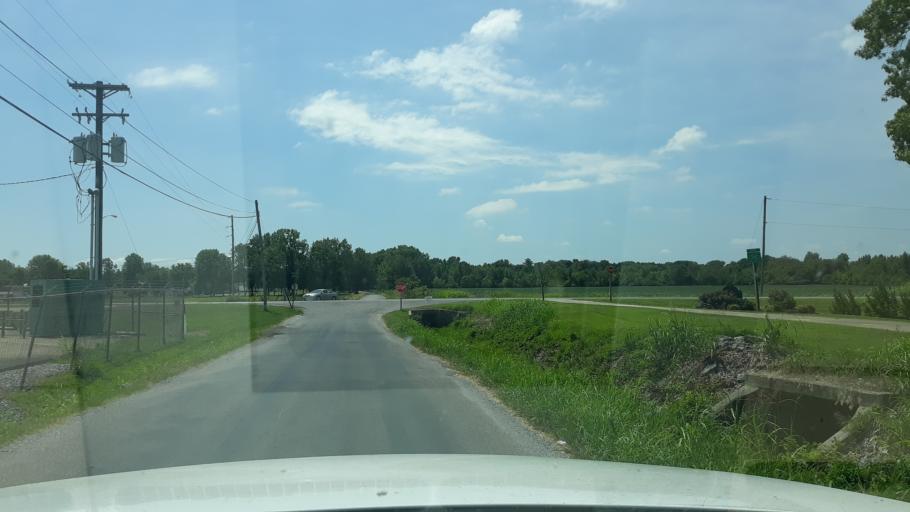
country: US
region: Illinois
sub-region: Saline County
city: Eldorado
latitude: 37.8040
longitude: -88.4322
